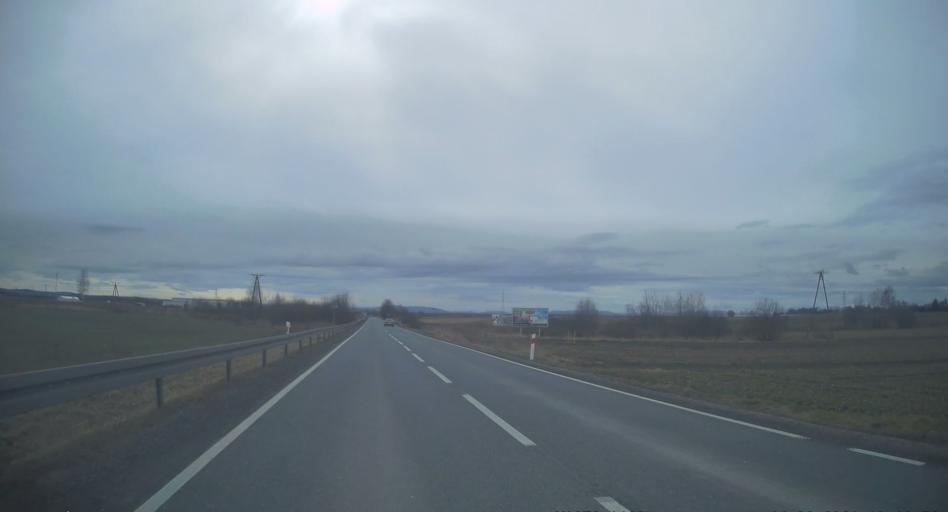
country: PL
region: Lesser Poland Voivodeship
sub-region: Powiat wielicki
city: Szarow
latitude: 49.9970
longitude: 20.2769
